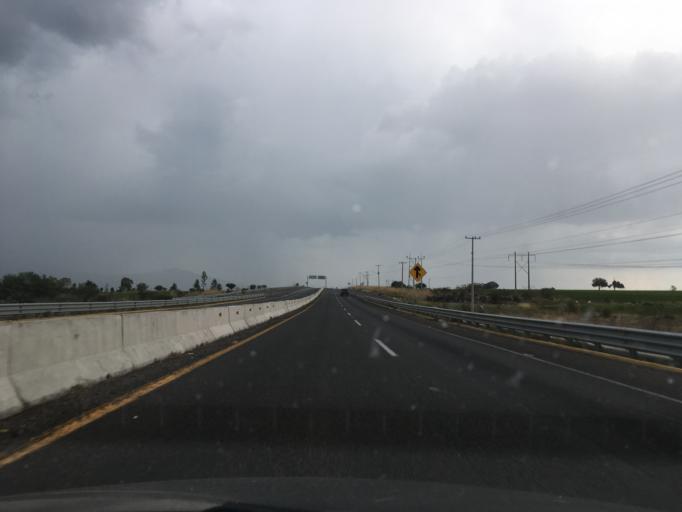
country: MX
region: Guanajuato
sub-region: Tarimoro
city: San Juan Bautista Cacalote
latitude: 20.3434
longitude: -100.8059
